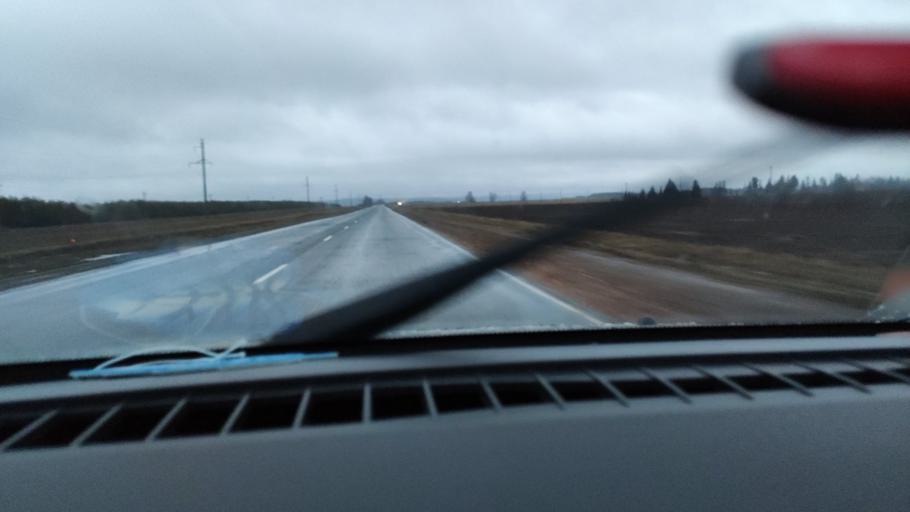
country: RU
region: Udmurtiya
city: Alnashi
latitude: 56.2065
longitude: 52.4438
